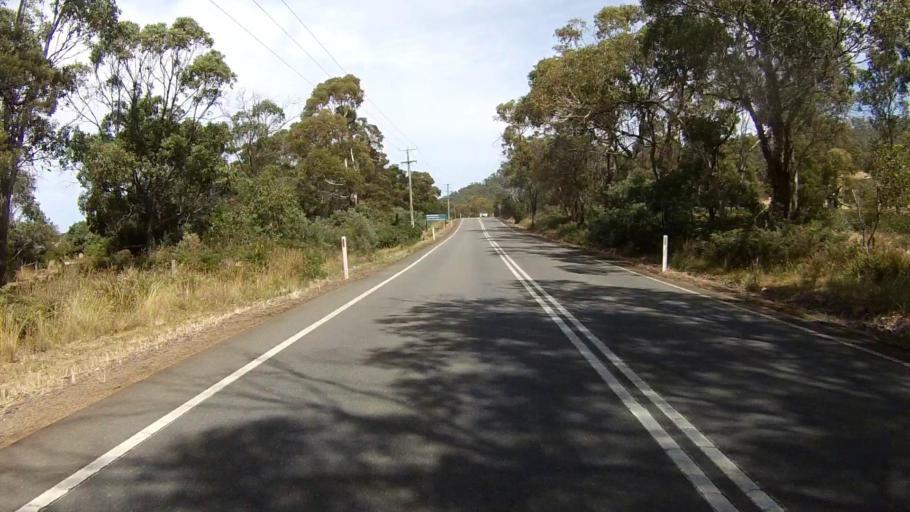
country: AU
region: Tasmania
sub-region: Clarence
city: Sandford
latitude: -43.0139
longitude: 147.4909
